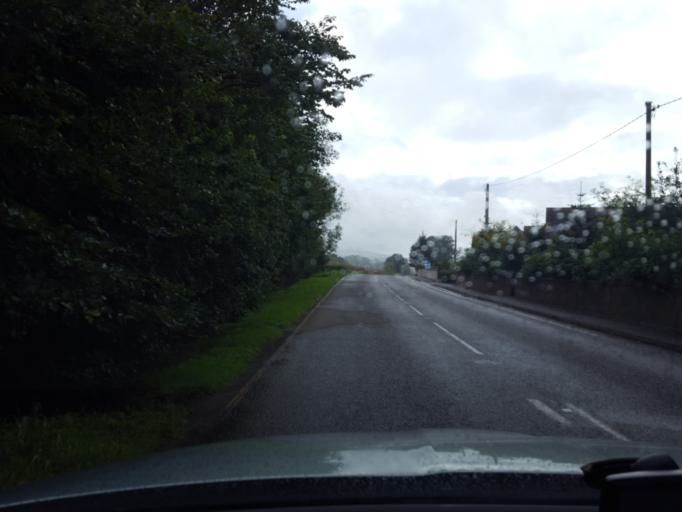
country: GB
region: Scotland
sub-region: Aberdeenshire
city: Laurencekirk
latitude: 56.8760
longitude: -2.4075
